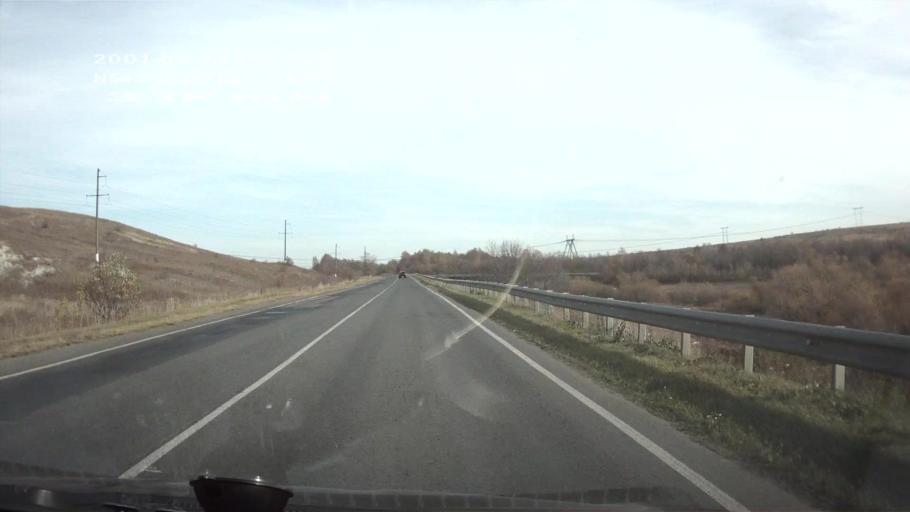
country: RU
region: Mordoviya
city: Atyashevo
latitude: 54.5320
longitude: 45.9187
